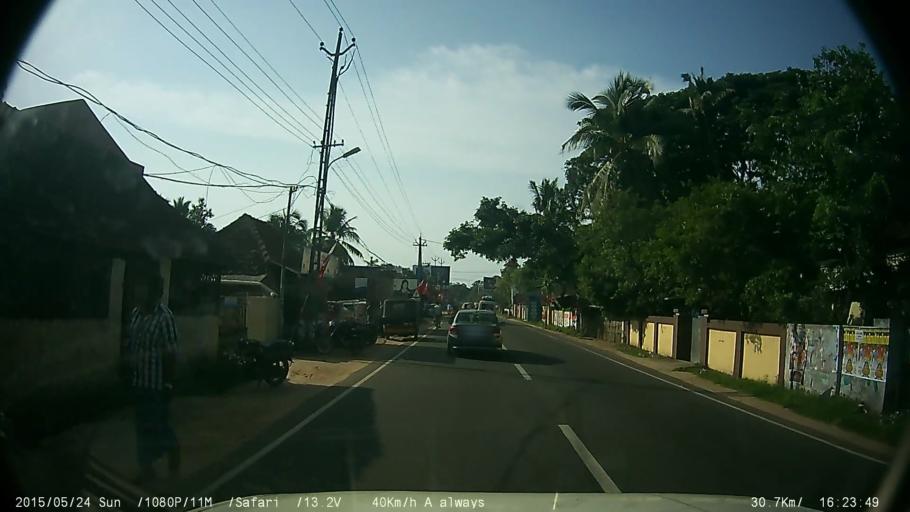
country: IN
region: Kerala
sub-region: Alappuzha
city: Alleppey
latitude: 9.5031
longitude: 76.3286
